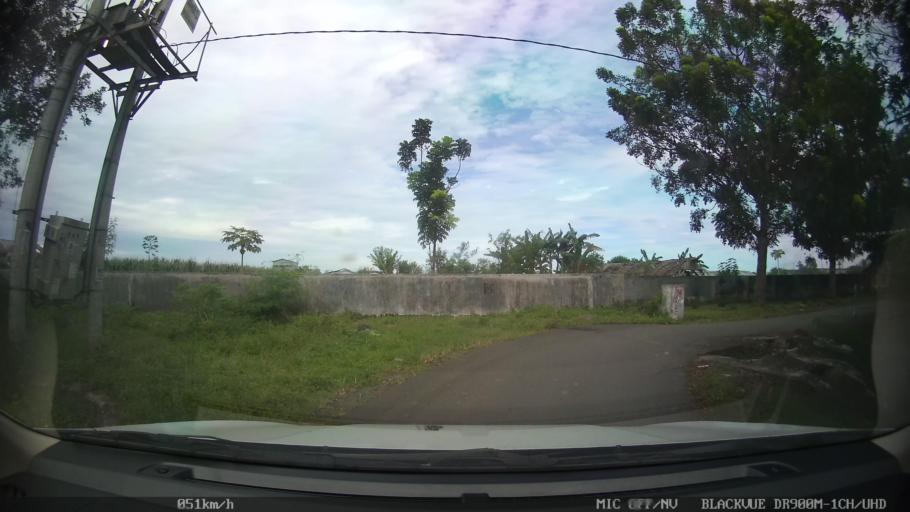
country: ID
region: North Sumatra
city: Sunggal
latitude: 3.5865
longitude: 98.5799
